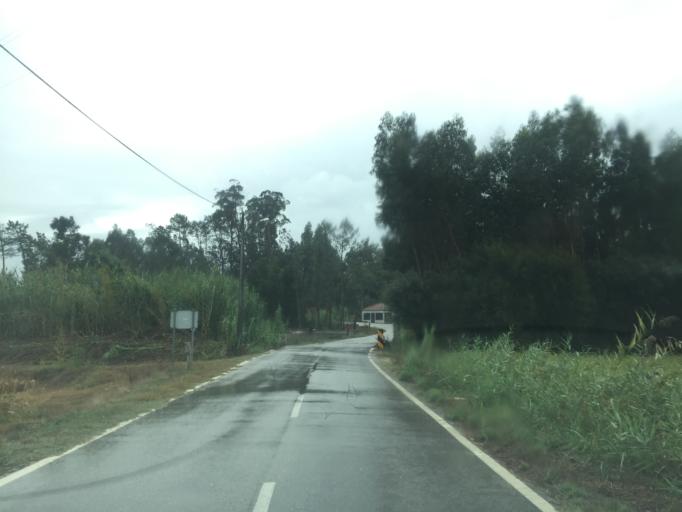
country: PT
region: Coimbra
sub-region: Figueira da Foz
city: Lavos
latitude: 40.0649
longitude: -8.7761
